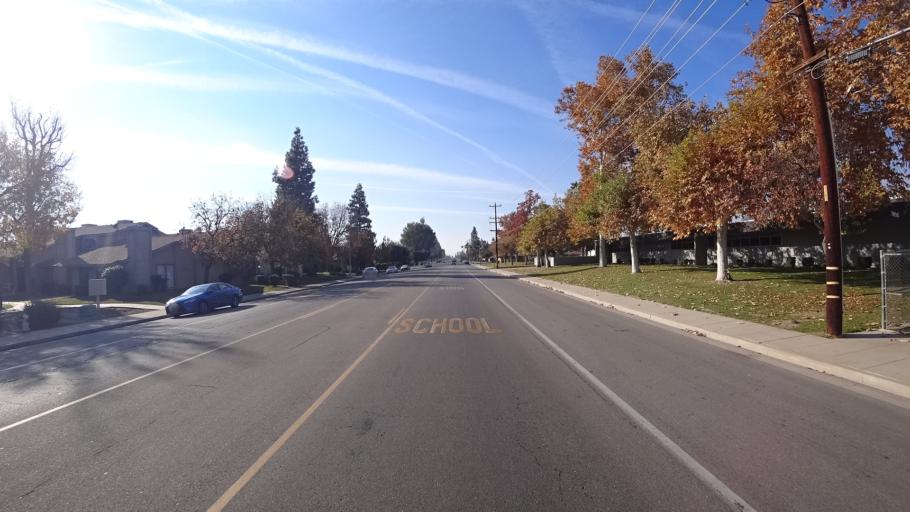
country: US
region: California
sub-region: Kern County
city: Bakersfield
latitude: 35.3251
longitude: -119.0508
